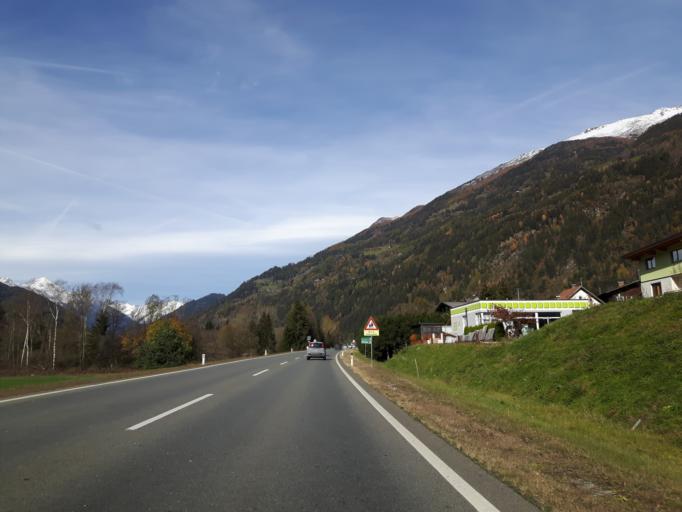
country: AT
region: Tyrol
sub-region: Politischer Bezirk Lienz
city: Ainet
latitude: 46.8625
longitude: 12.6891
